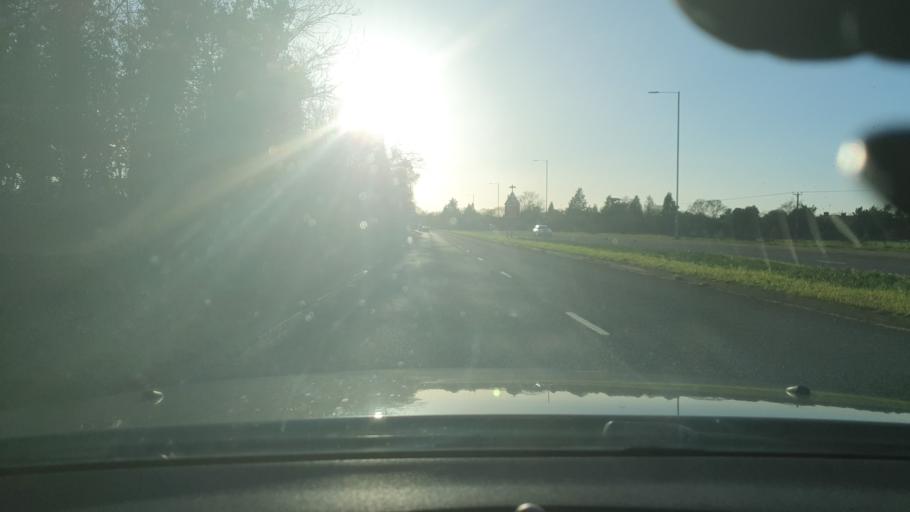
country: GB
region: England
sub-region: Wokingham
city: Charvil
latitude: 51.4702
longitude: -0.8985
